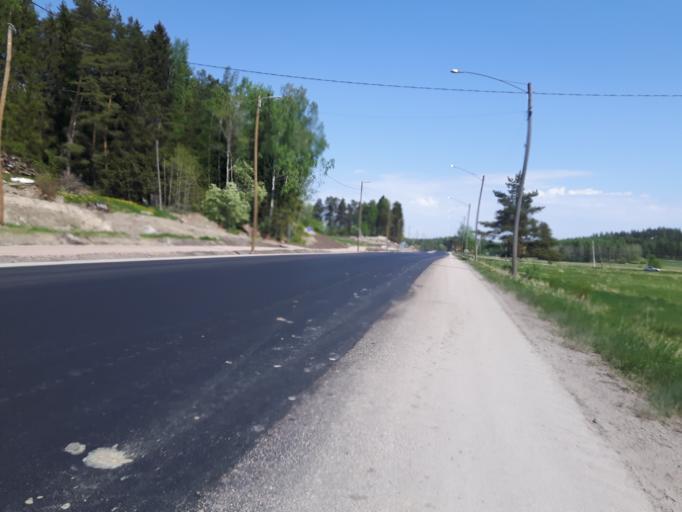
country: FI
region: Uusimaa
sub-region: Porvoo
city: Porvoo
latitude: 60.3482
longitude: 25.4957
